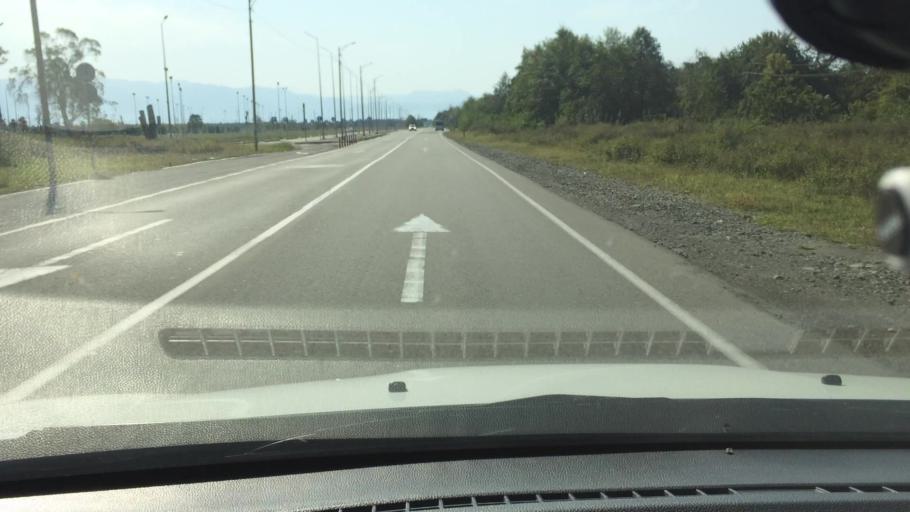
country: GE
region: Guria
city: Urek'i
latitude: 41.9416
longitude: 41.7708
